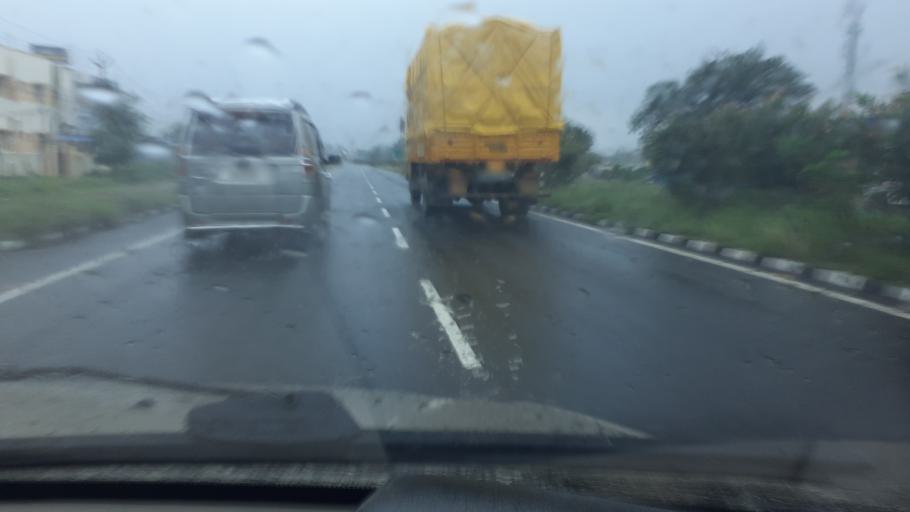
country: IN
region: Tamil Nadu
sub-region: Virudhunagar
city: Virudunagar
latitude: 9.6077
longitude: 77.9557
